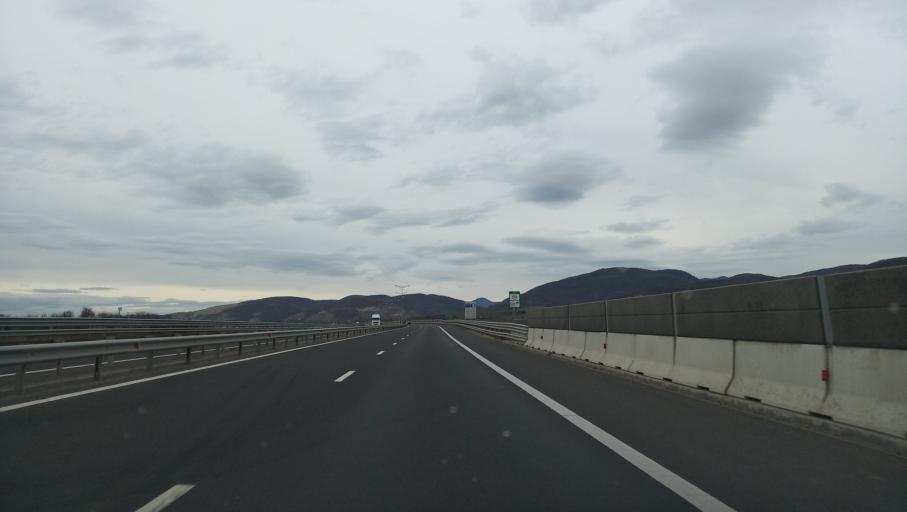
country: RO
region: Hunedoara
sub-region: Oras Simeria
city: Simeria
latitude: 45.8606
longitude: 23.0276
